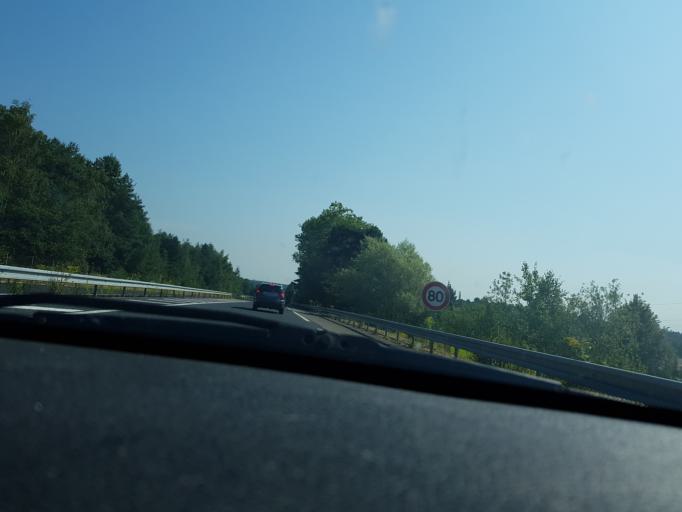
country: FR
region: Lorraine
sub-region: Departement de la Moselle
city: Longeville-les-Saint-Avold
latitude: 49.1064
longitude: 6.6490
